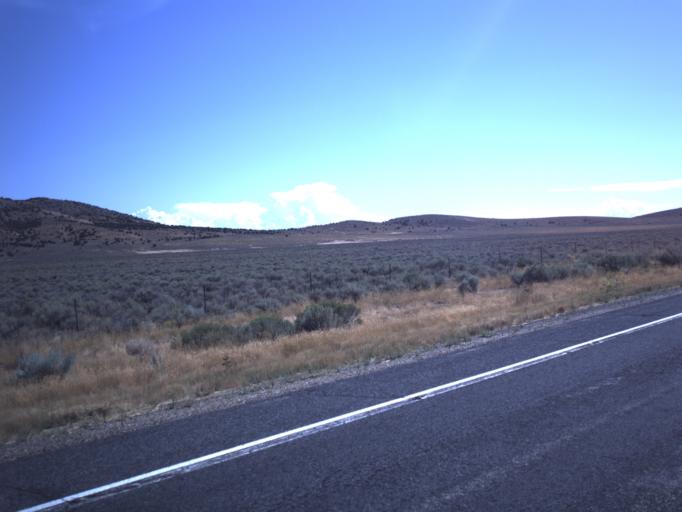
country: US
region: Utah
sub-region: Utah County
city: Eagle Mountain
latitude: 40.0788
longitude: -112.3982
